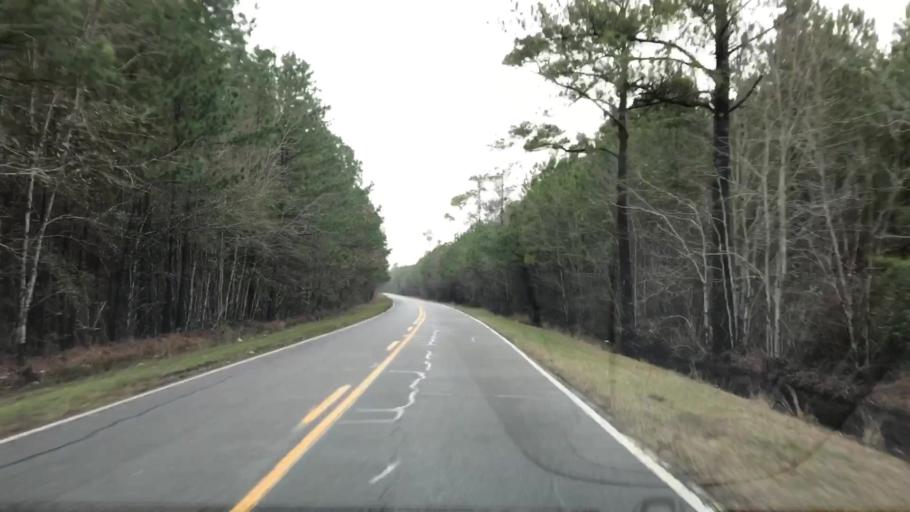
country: US
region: South Carolina
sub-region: Georgetown County
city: Murrells Inlet
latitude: 33.6316
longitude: -79.2500
